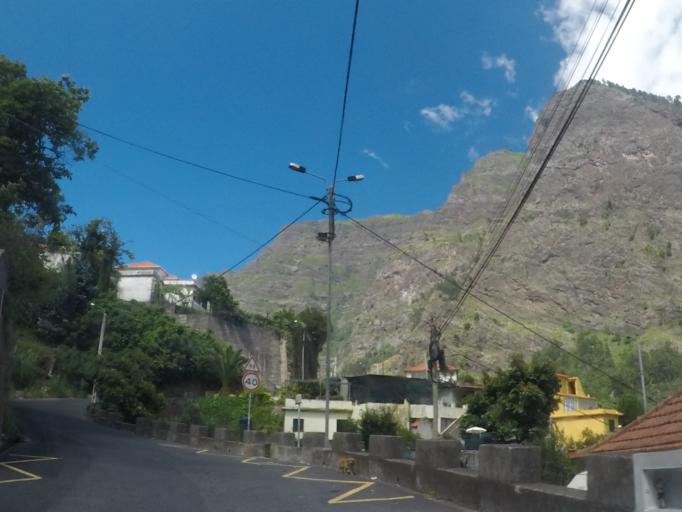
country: PT
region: Madeira
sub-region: Camara de Lobos
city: Curral das Freiras
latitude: 32.7082
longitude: -16.9740
